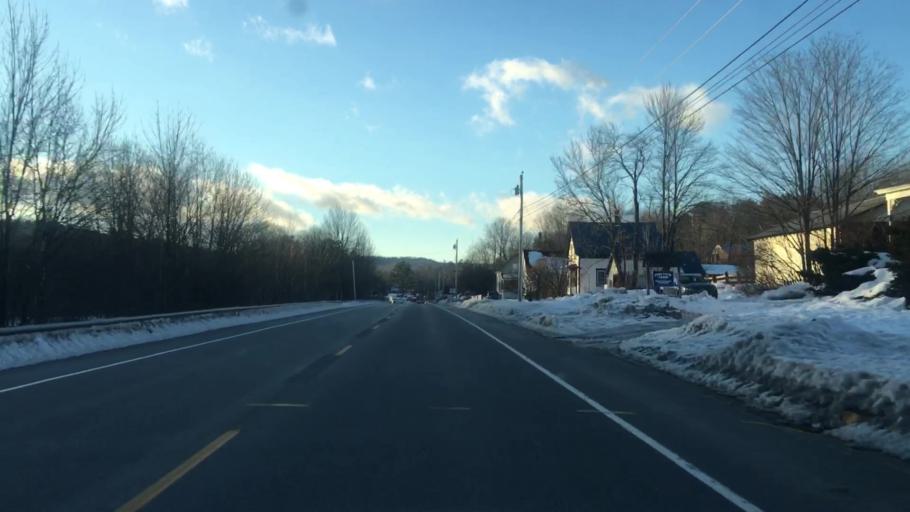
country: US
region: Maine
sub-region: Franklin County
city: Wilton
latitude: 44.5744
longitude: -70.3100
